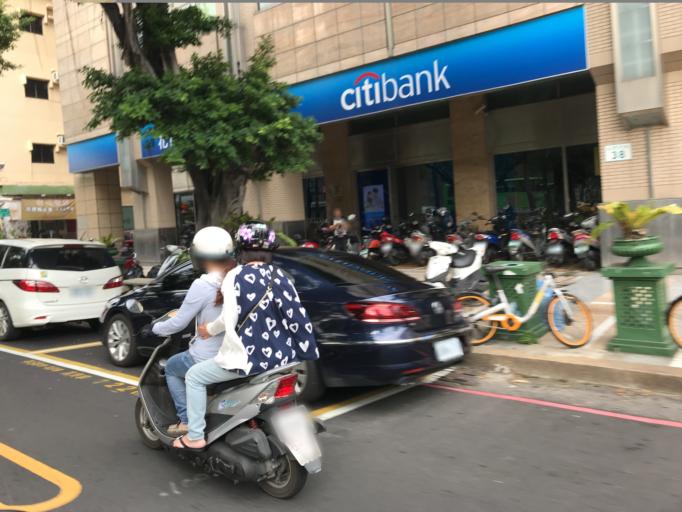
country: TW
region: Kaohsiung
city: Kaohsiung
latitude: 22.6312
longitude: 120.3136
